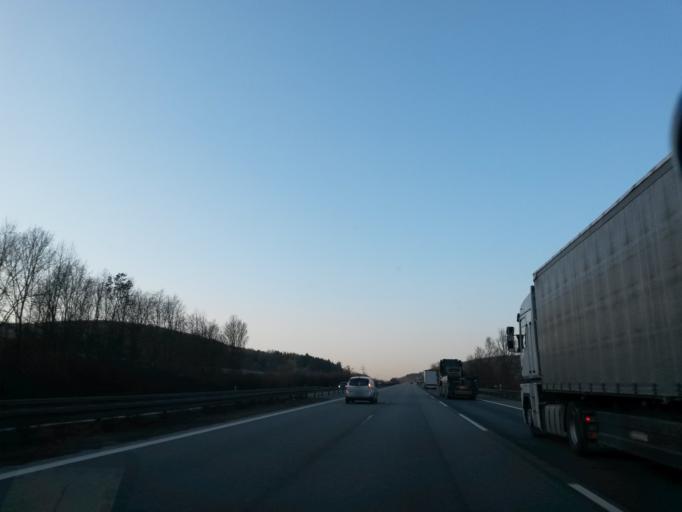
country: DE
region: Bavaria
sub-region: Regierungsbezirk Mittelfranken
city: Thalmassing
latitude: 49.0870
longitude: 11.2881
